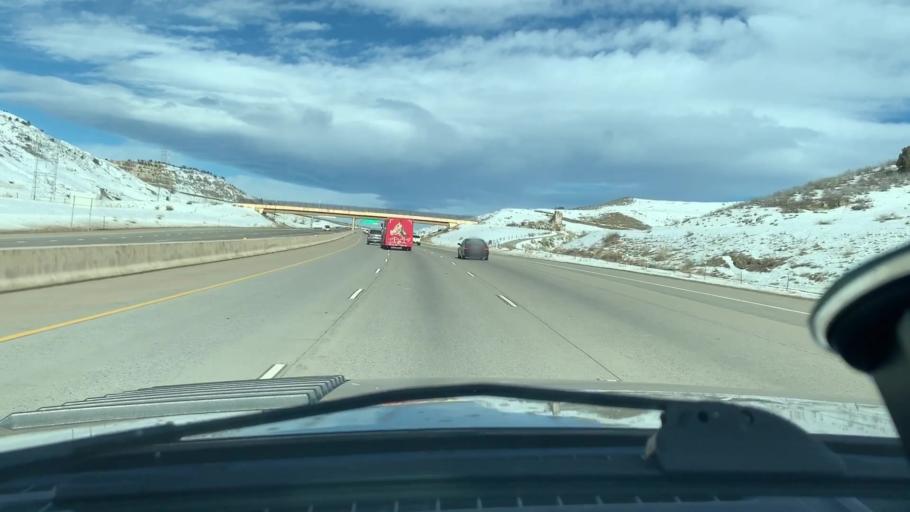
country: US
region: Colorado
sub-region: Jefferson County
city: West Pleasant View
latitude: 39.6934
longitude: -105.1888
